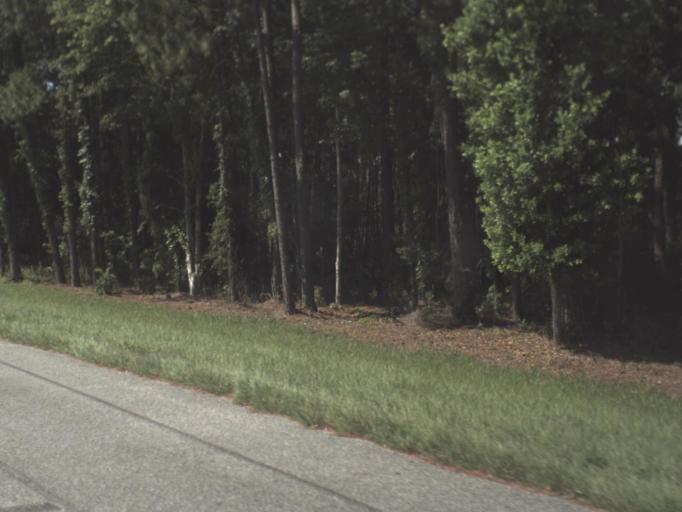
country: US
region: Florida
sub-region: Saint Johns County
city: Fruit Cove
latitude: 30.0364
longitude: -81.4924
